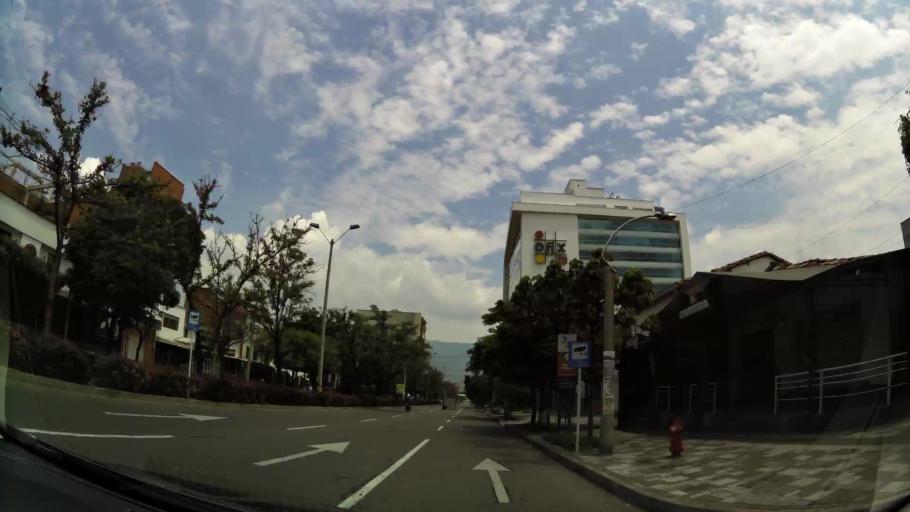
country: CO
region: Antioquia
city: Medellin
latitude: 6.2387
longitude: -75.6015
